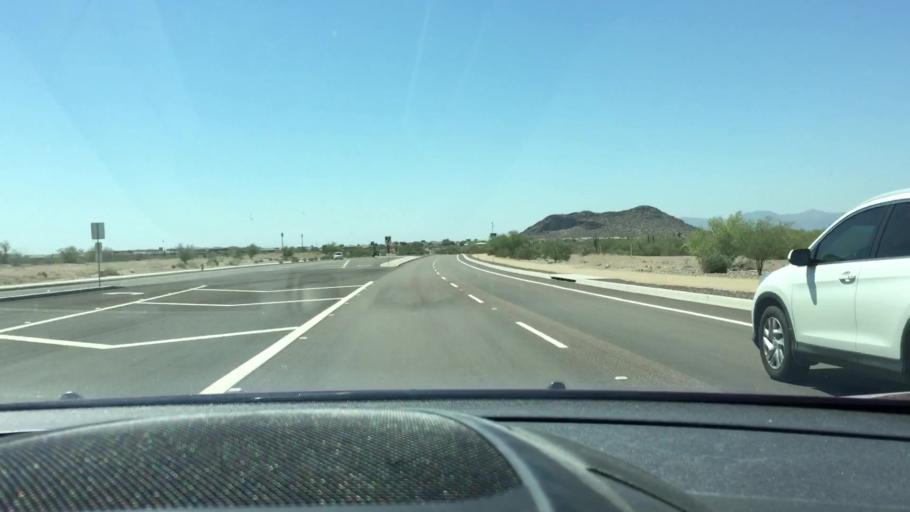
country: US
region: Arizona
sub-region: Maricopa County
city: Sun City West
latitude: 33.7480
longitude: -112.2578
